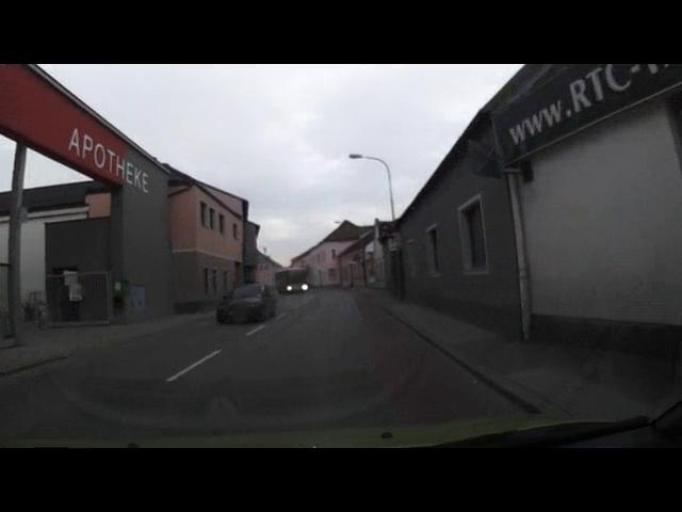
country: AT
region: Lower Austria
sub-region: Politischer Bezirk Wiener Neustadt
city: Ebenfurth
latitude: 47.8773
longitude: 16.3698
